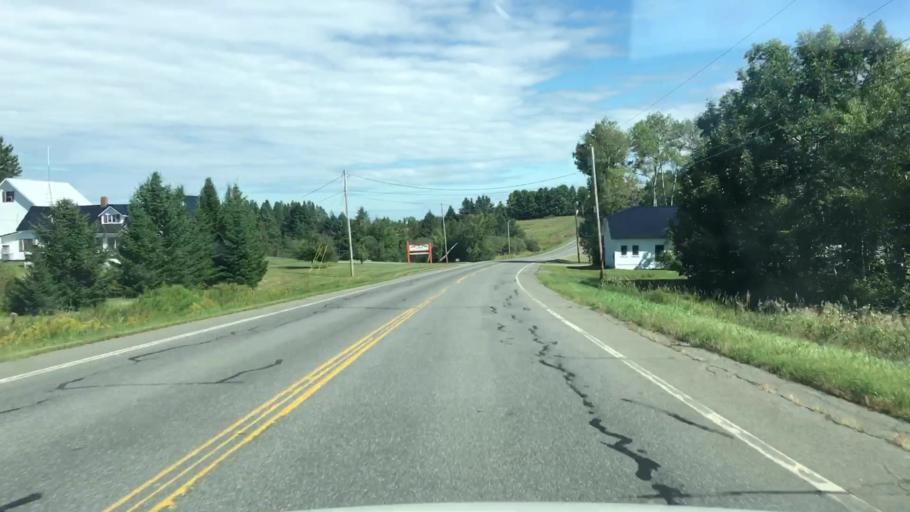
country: US
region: Maine
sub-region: Penobscot County
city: Dexter
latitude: 45.0713
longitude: -69.2373
